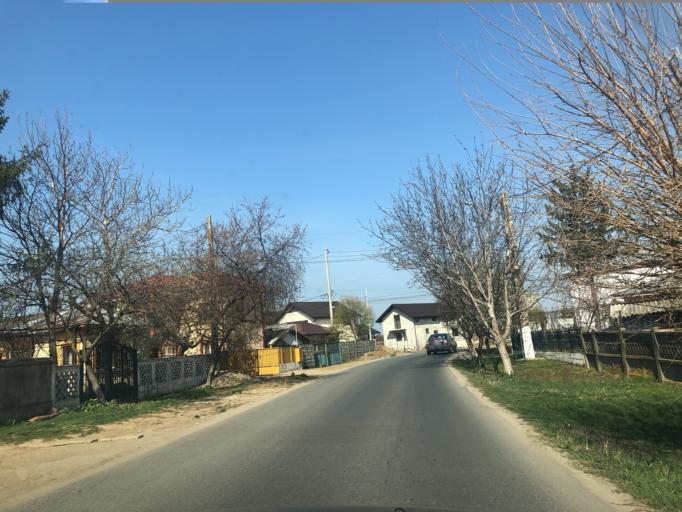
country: RO
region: Ilfov
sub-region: Comuna Clinceni
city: Clinceni
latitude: 44.3768
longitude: 25.9520
